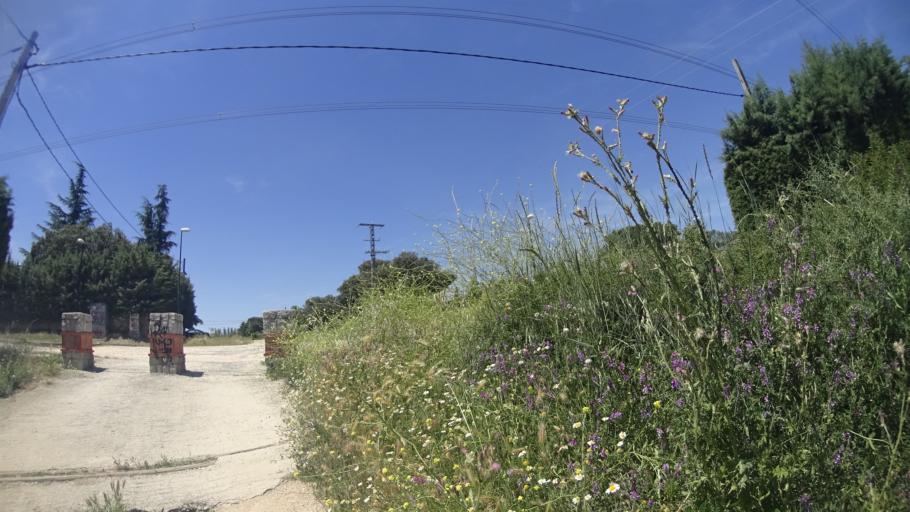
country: ES
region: Madrid
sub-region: Provincia de Madrid
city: Navalquejigo
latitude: 40.6203
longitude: -4.0328
